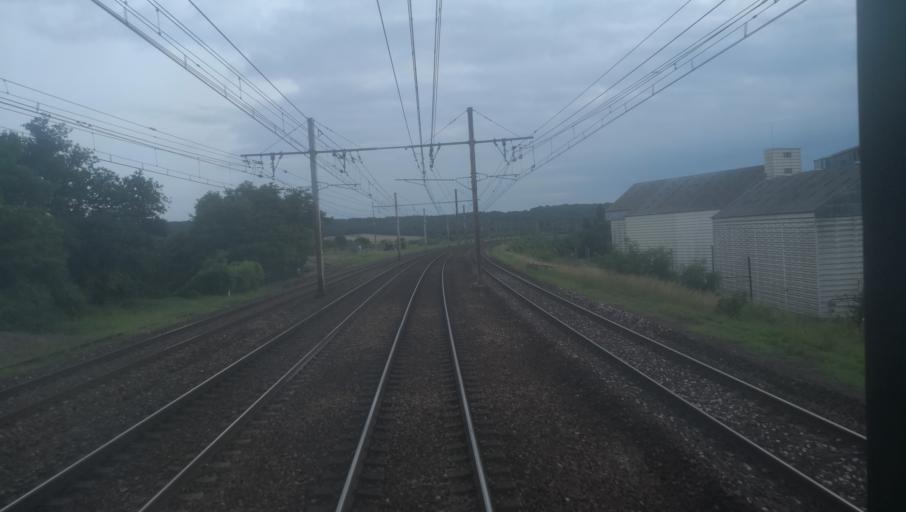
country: FR
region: Ile-de-France
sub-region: Departement de l'Essonne
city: Morigny-Champigny
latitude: 48.4519
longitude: 2.1679
